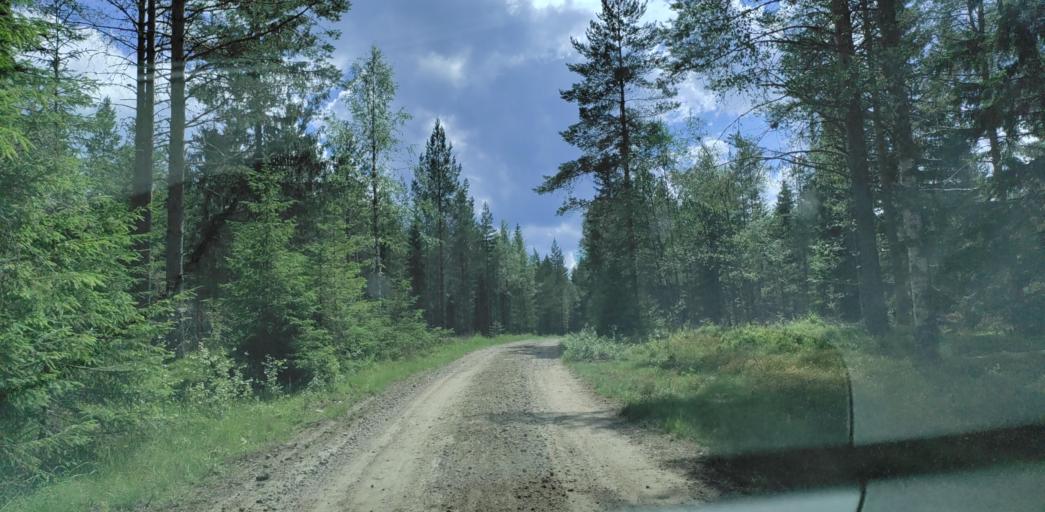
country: SE
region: Vaermland
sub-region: Hagfors Kommun
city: Ekshaerad
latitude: 60.0724
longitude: 13.3459
